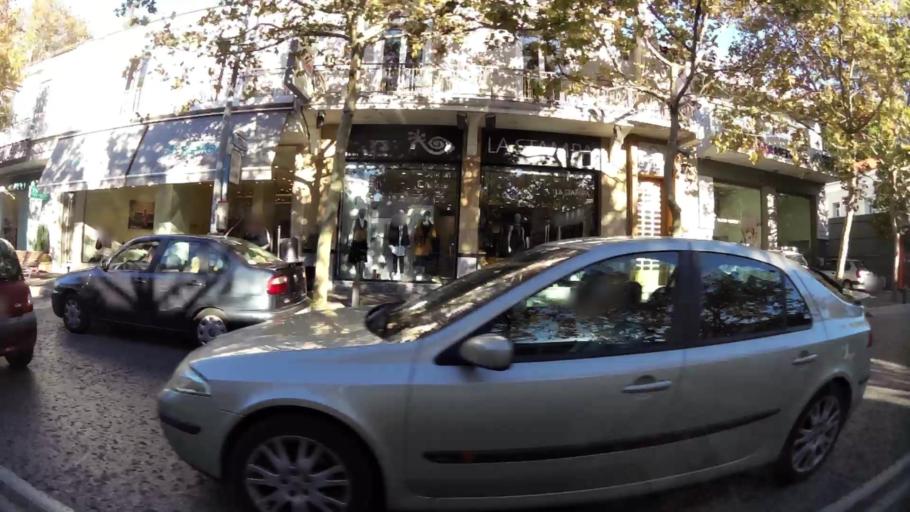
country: GR
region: Attica
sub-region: Nomarchia Athinas
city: Kifisia
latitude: 38.0746
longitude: 23.8124
